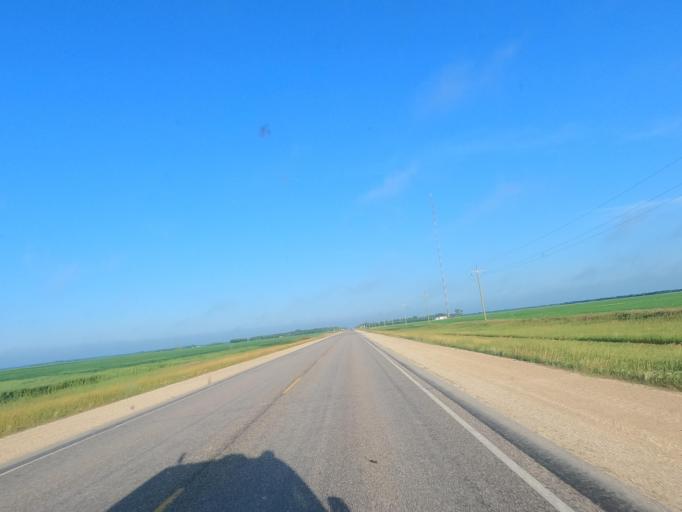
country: CA
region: Manitoba
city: Headingley
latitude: 49.7685
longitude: -97.4959
